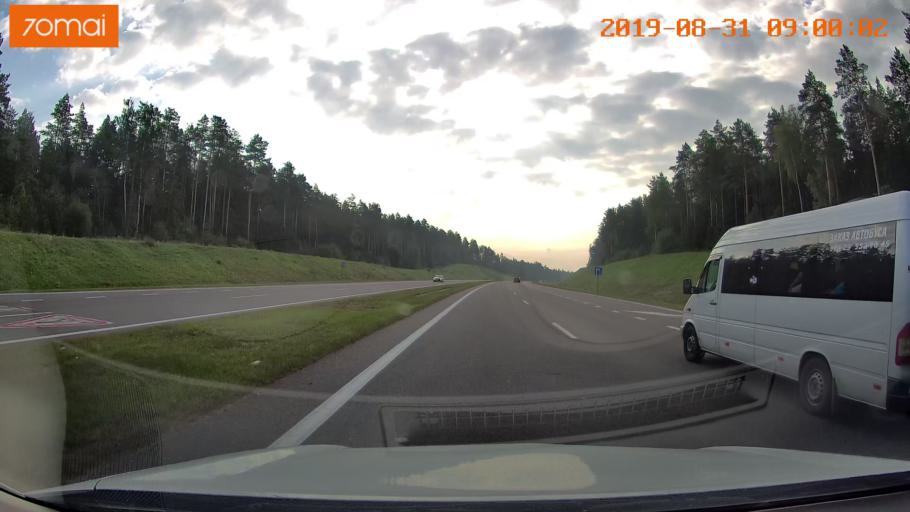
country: BY
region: Minsk
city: Chervyen'
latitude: 53.7624
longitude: 28.2258
